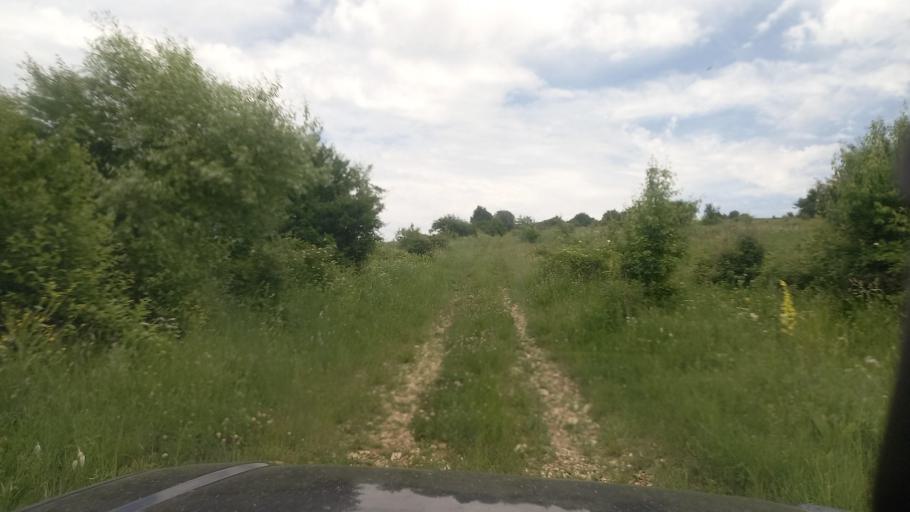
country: RU
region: Karachayevo-Cherkesiya
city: Pregradnaya
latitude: 44.0857
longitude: 41.2125
